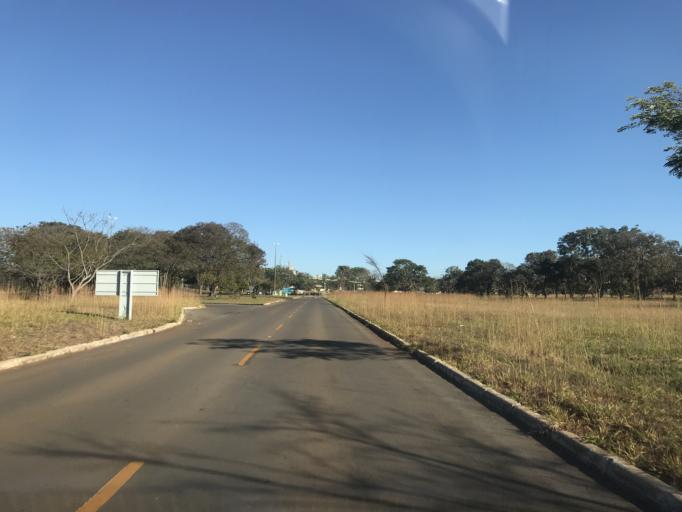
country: BR
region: Federal District
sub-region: Brasilia
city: Brasilia
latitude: -15.8309
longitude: -47.8993
